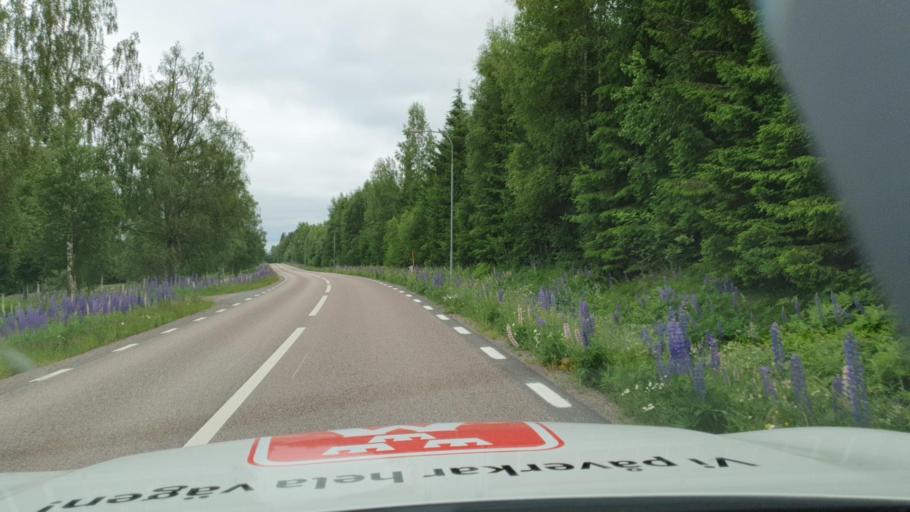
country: SE
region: Vaermland
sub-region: Sunne Kommun
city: Sunne
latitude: 59.8809
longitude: 12.9272
